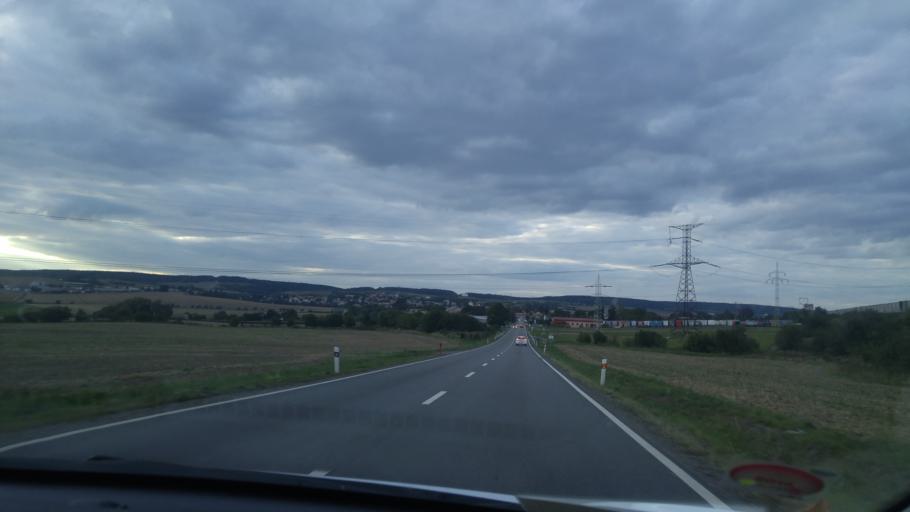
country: CZ
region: South Moravian
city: Ricany
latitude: 49.2021
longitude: 16.4202
